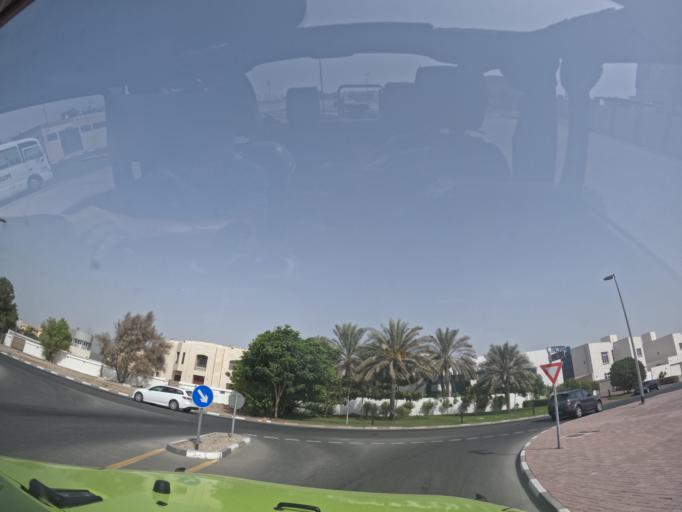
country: AE
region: Dubai
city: Dubai
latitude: 25.1451
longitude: 55.2168
